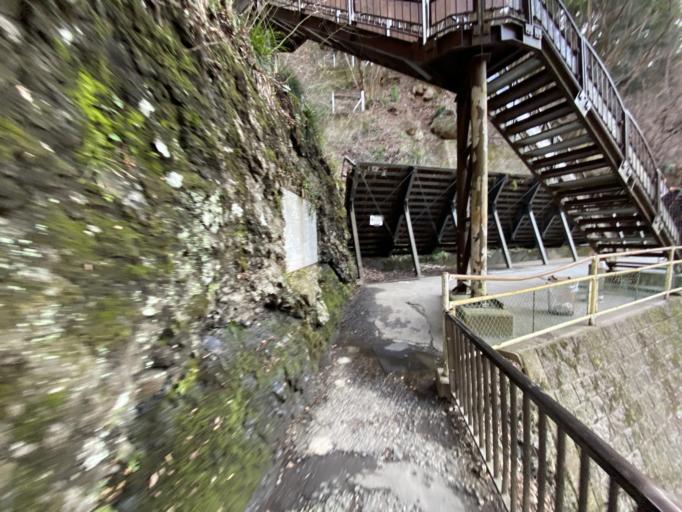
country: JP
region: Ibaraki
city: Daigo
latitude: 36.7641
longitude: 140.4060
